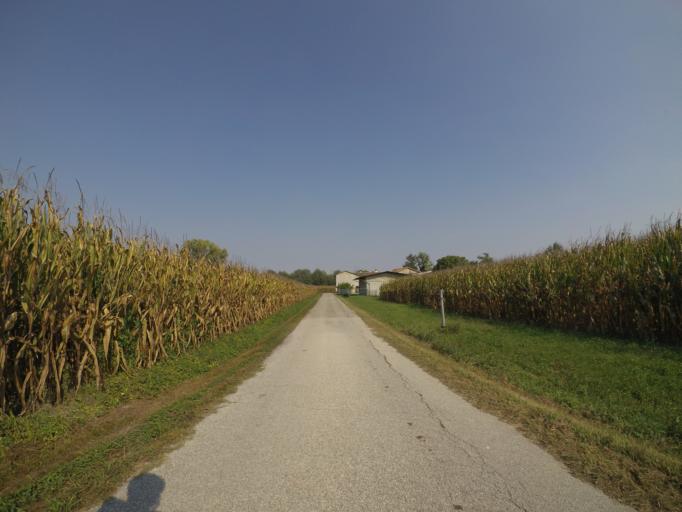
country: IT
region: Friuli Venezia Giulia
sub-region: Provincia di Udine
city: Camino al Tagliamento
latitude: 45.9098
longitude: 12.9323
